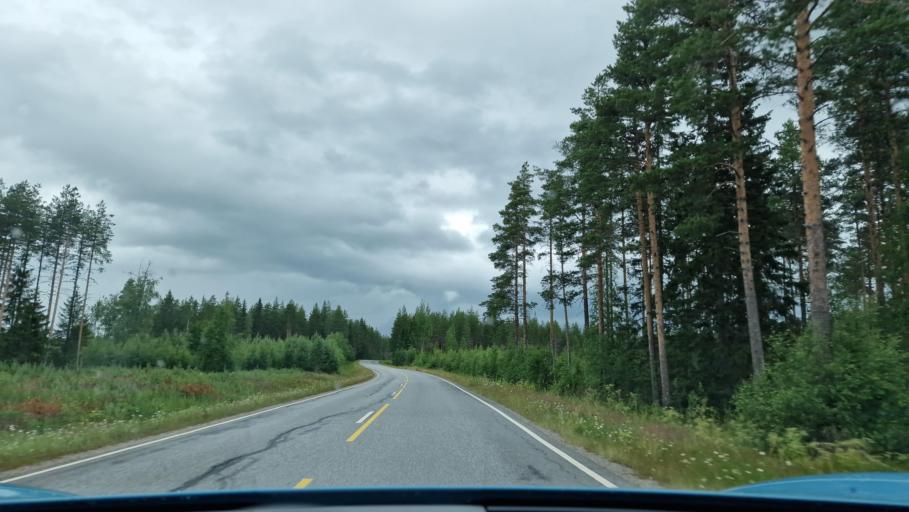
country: FI
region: Southern Ostrobothnia
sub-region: Jaerviseutu
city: Soini
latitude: 62.7519
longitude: 24.4021
